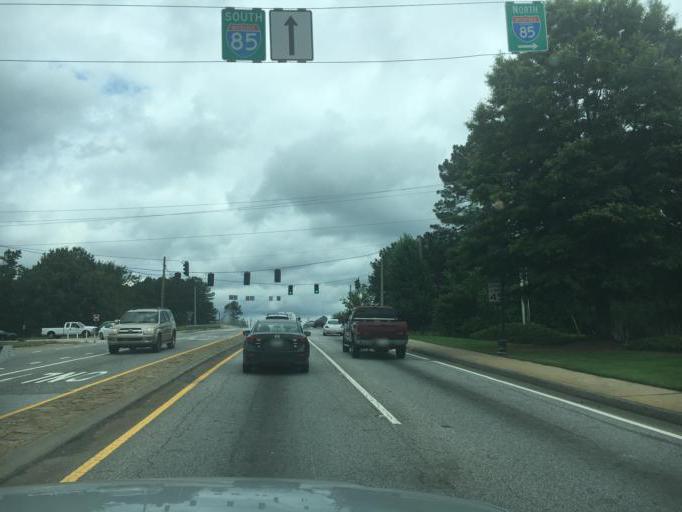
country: US
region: Georgia
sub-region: Gwinnett County
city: Dacula
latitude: 34.0734
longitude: -83.9177
